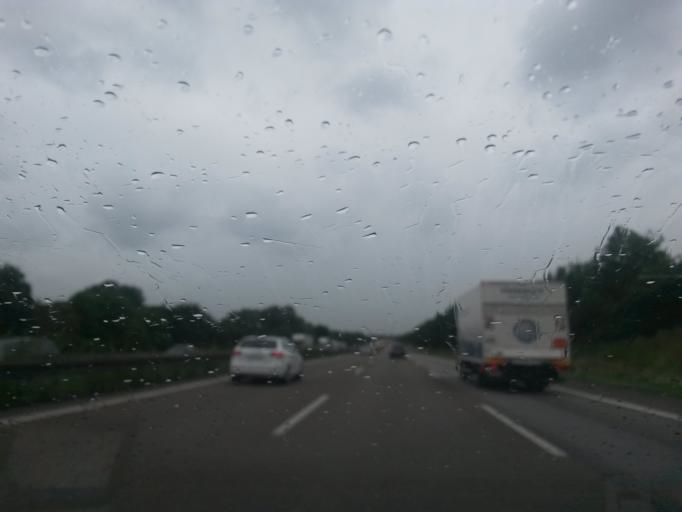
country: DE
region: Bavaria
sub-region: Upper Bavaria
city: Manching
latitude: 48.7297
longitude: 11.4733
